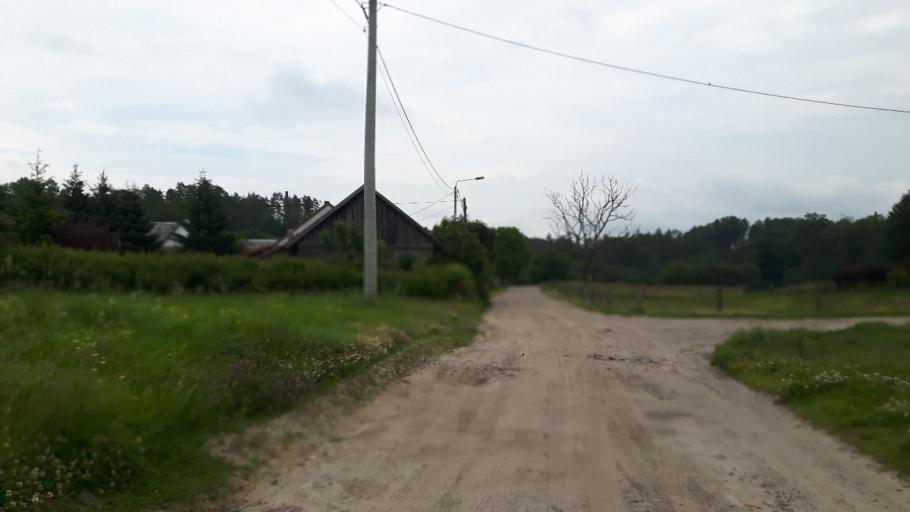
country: PL
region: Warmian-Masurian Voivodeship
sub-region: Powiat braniewski
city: Frombork
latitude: 54.3147
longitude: 19.6101
